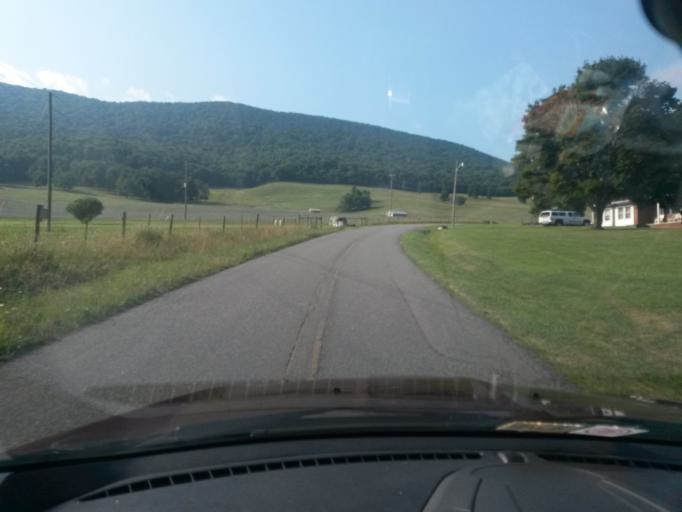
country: US
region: Virginia
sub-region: Giles County
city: Narrows
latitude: 37.3779
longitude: -80.7936
